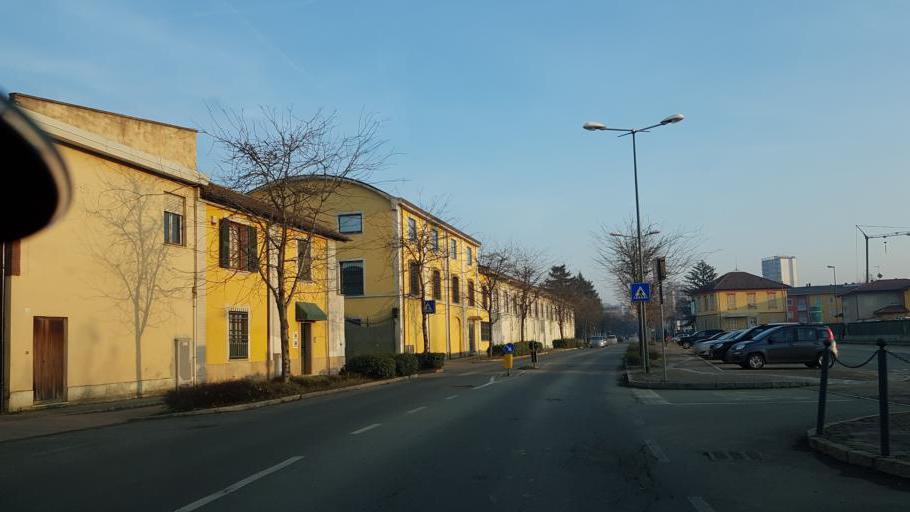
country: IT
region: Piedmont
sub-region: Provincia di Alessandria
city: Novi Ligure
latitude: 44.7665
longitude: 8.7780
